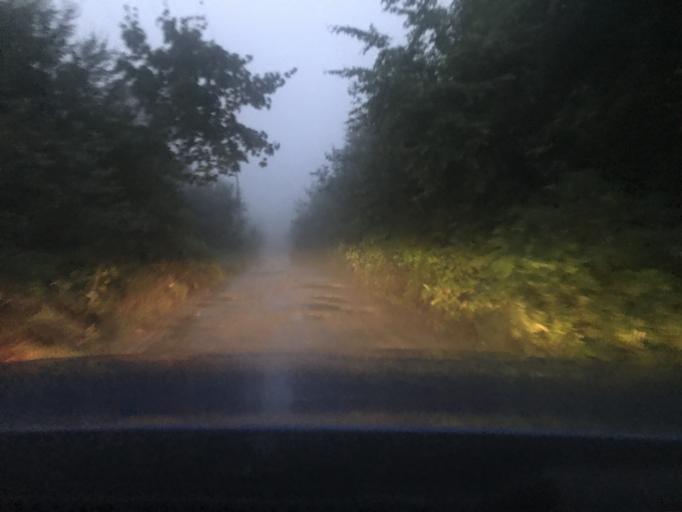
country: TR
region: Trabzon
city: Hayrat
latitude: 40.8287
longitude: 40.3880
